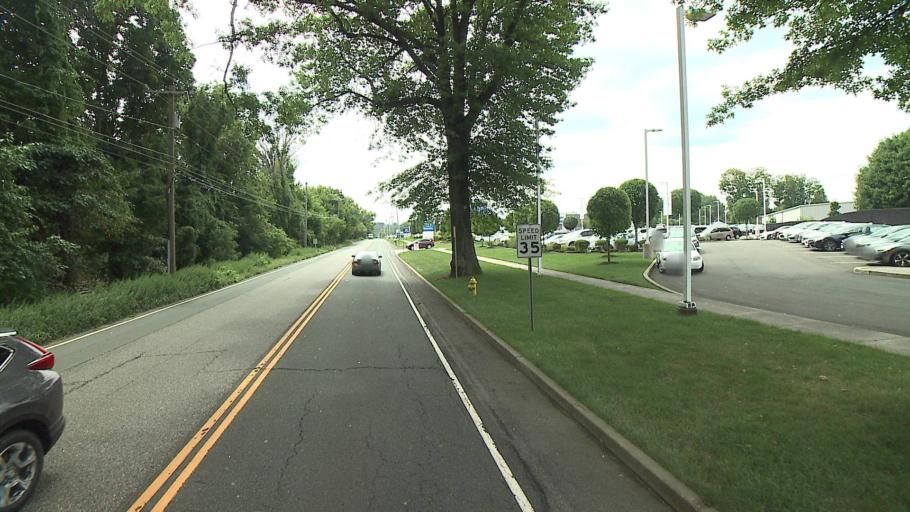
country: US
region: Connecticut
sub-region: Fairfield County
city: Danbury
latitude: 41.4164
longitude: -73.4218
